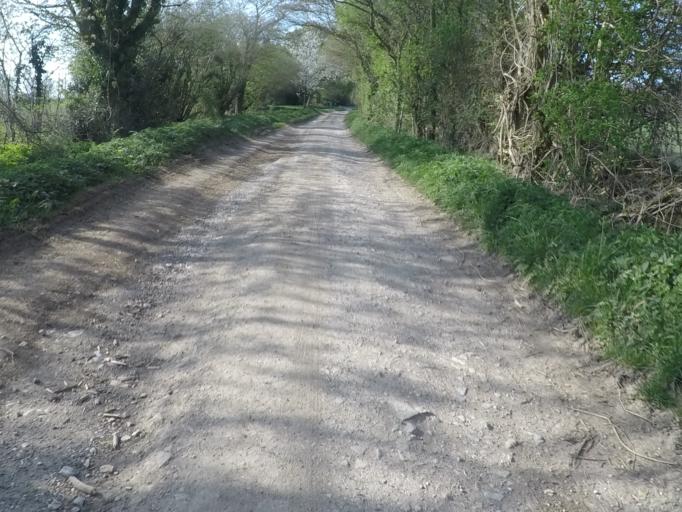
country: GB
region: England
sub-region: Oxfordshire
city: Charlbury
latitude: 51.8886
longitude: -1.4566
